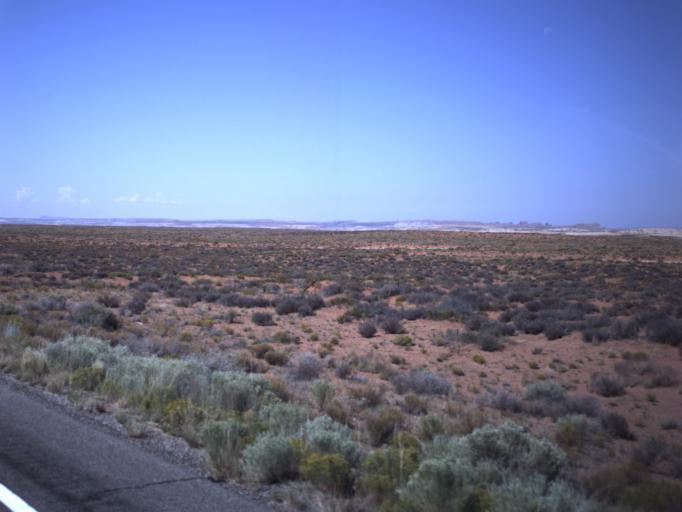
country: US
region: Utah
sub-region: San Juan County
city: Blanding
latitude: 37.0330
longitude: -109.5920
